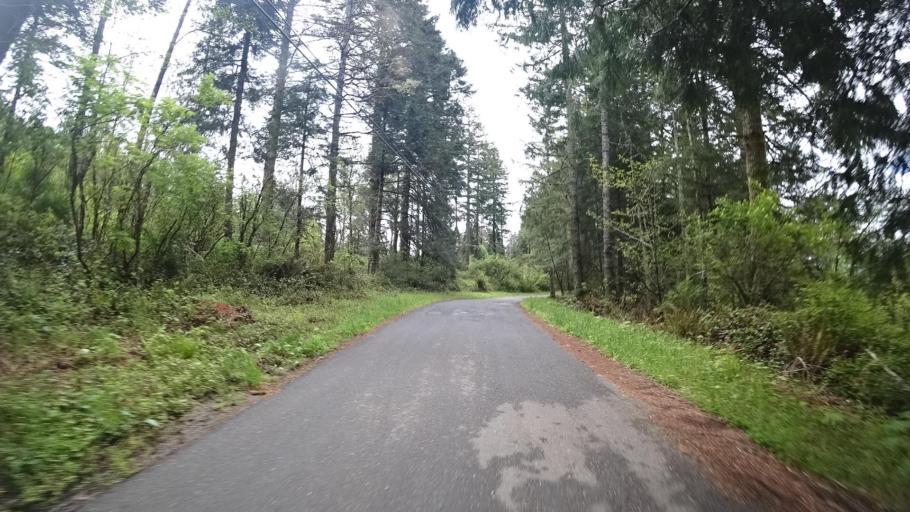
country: US
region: California
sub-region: Humboldt County
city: Bayside
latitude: 40.8314
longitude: -124.0124
